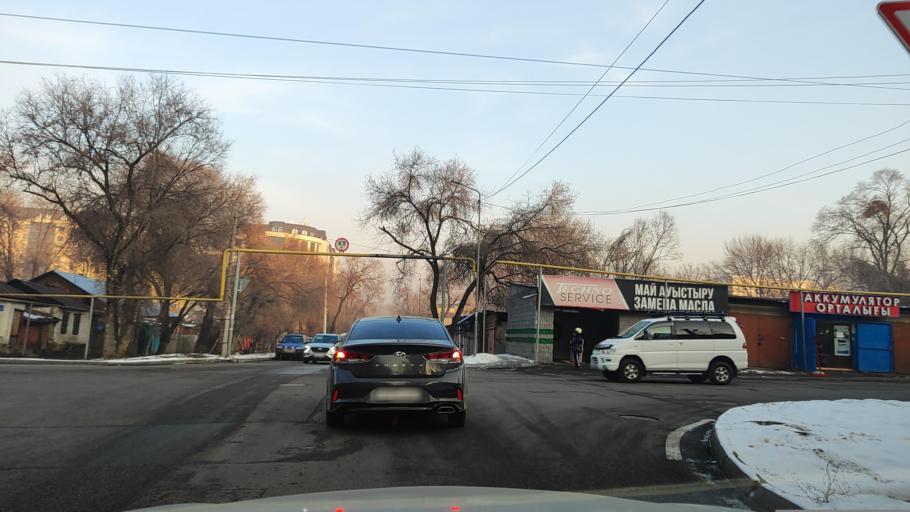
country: KZ
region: Almaty Qalasy
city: Almaty
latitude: 43.2575
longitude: 76.9600
